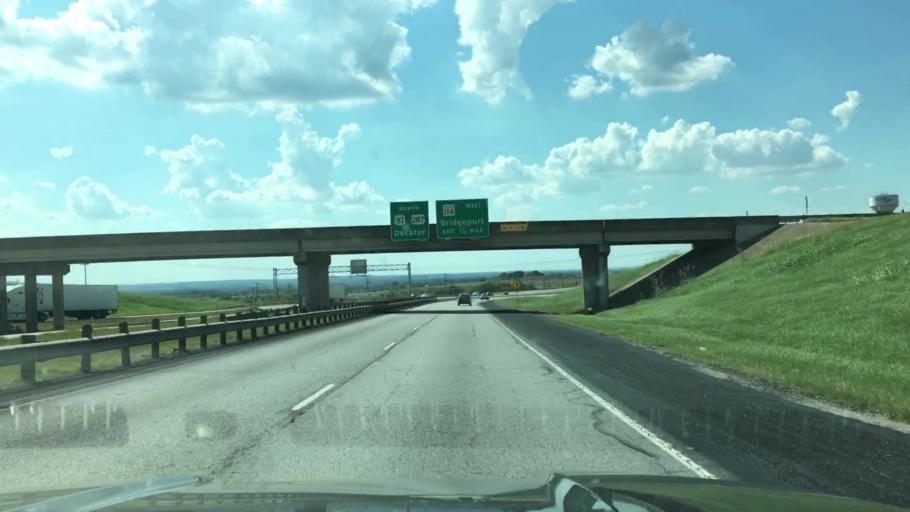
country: US
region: Texas
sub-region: Wise County
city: Rhome
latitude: 33.0464
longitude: -97.4707
